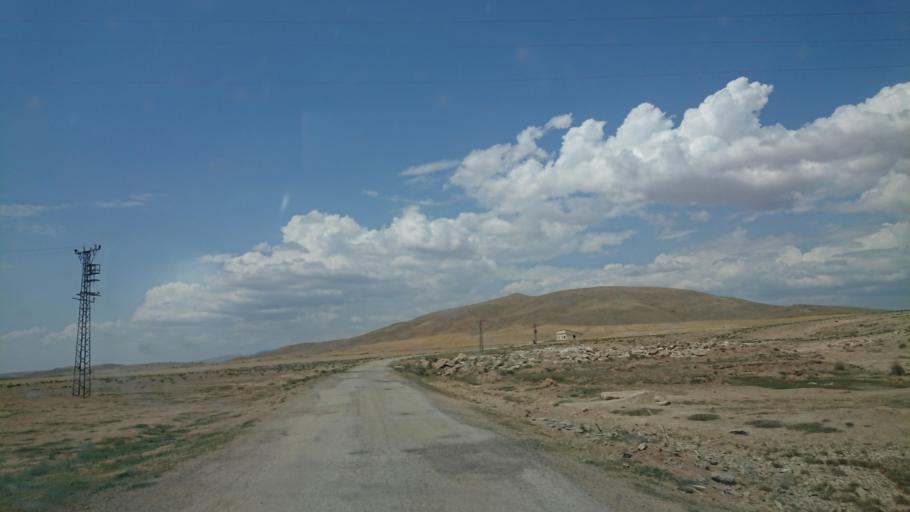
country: TR
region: Aksaray
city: Sariyahsi
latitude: 39.0027
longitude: 33.9109
